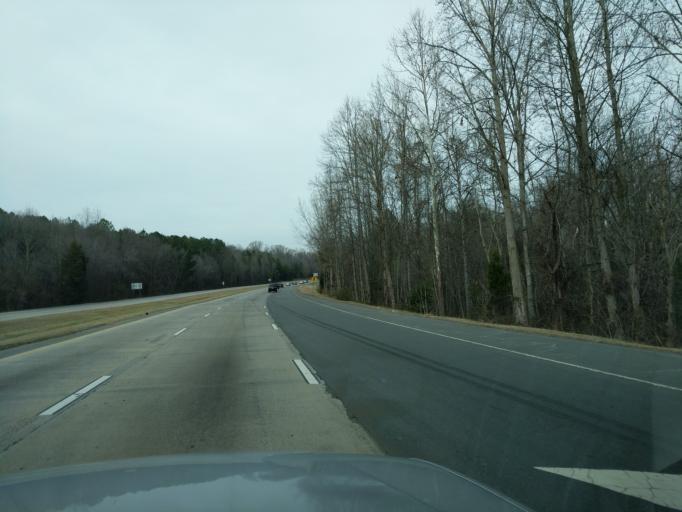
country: US
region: North Carolina
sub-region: Mecklenburg County
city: Charlotte
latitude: 35.1957
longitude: -80.9198
